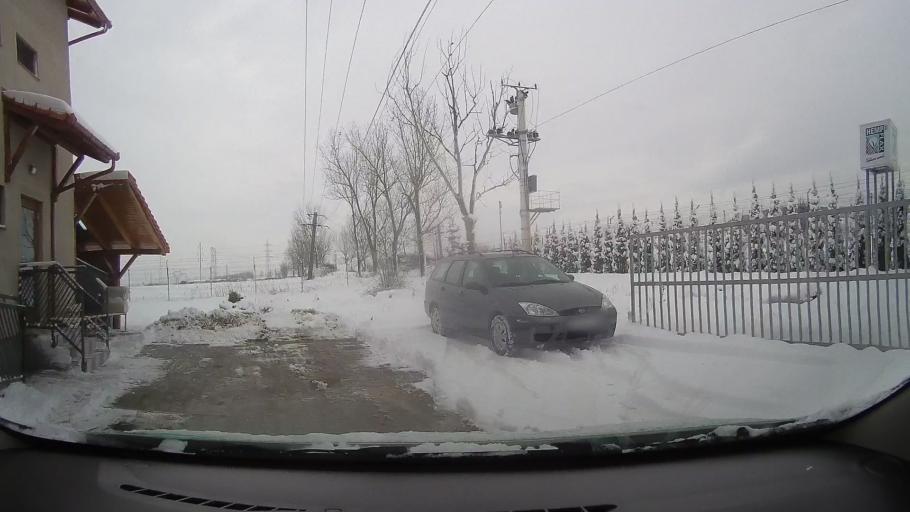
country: RO
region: Alba
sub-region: Comuna Pianu
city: Pianu de Jos
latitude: 45.9627
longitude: 23.5038
